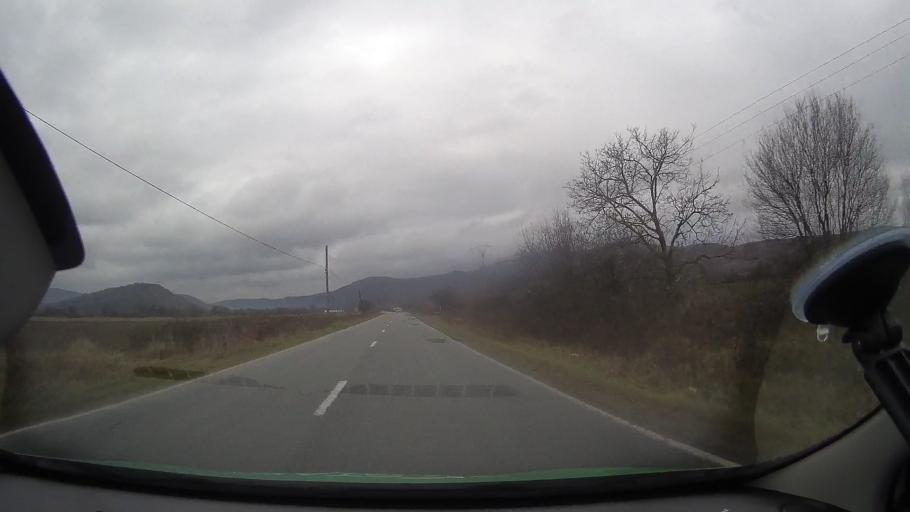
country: RO
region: Arad
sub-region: Comuna Buteni
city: Buteni
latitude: 46.3185
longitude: 22.1336
